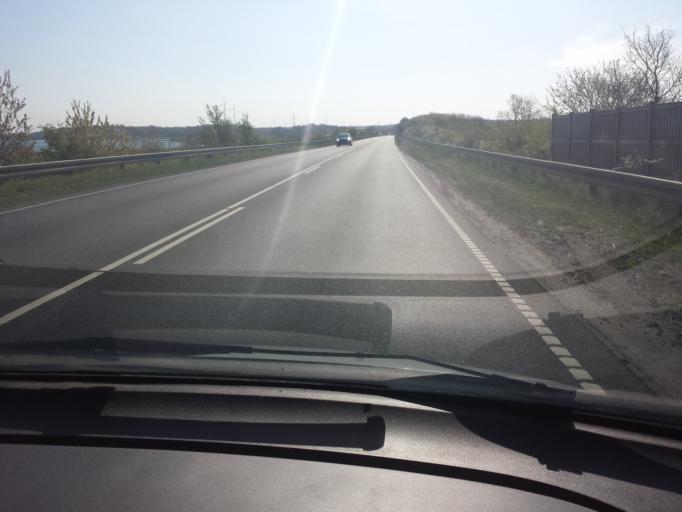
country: DK
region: South Denmark
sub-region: Sonderborg Kommune
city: Sonderborg
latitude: 54.9327
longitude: 9.8203
